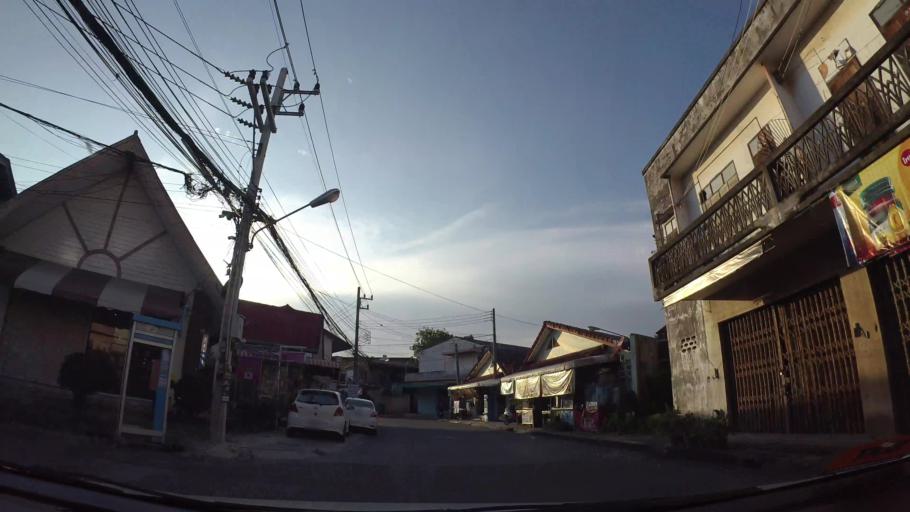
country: TH
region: Rayong
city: Rayong
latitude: 12.6839
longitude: 101.2798
